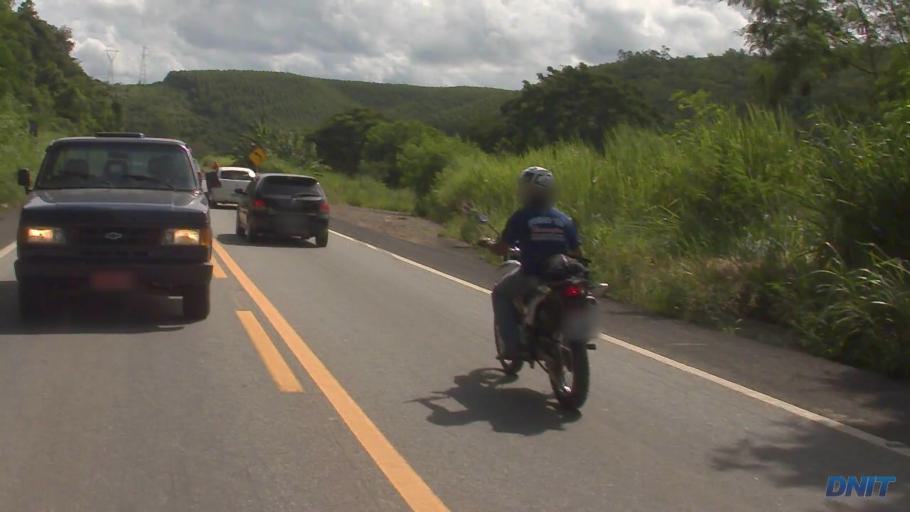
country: BR
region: Minas Gerais
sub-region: Ipaba
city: Ipaba
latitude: -19.3968
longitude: -42.4840
